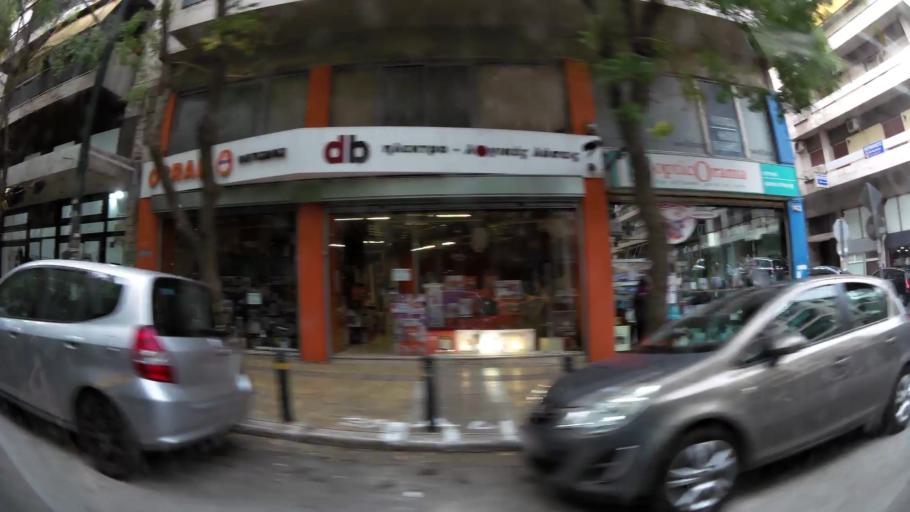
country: GR
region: Attica
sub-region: Nomarchia Athinas
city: Vyronas
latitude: 37.9618
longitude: 23.7440
